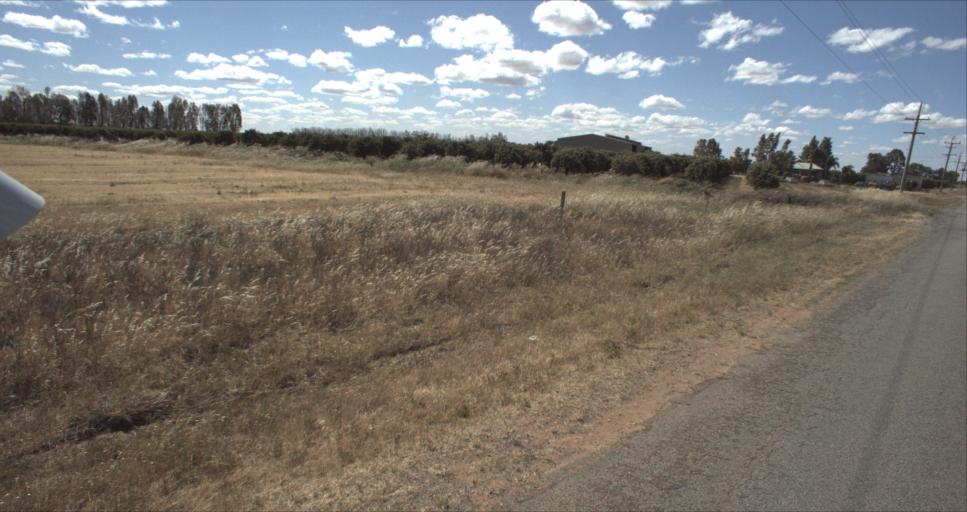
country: AU
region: New South Wales
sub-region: Leeton
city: Leeton
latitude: -34.5121
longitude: 146.2525
